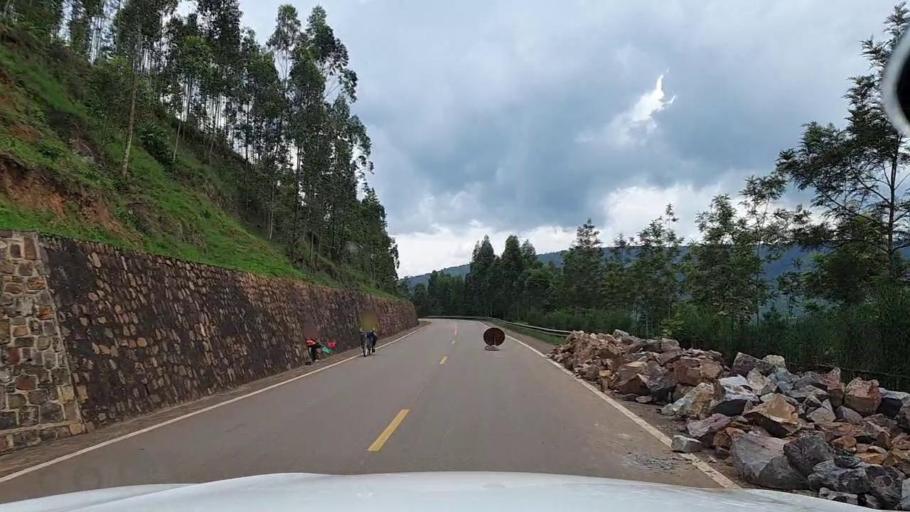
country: RW
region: Kigali
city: Kigali
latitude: -1.7905
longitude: 30.1284
